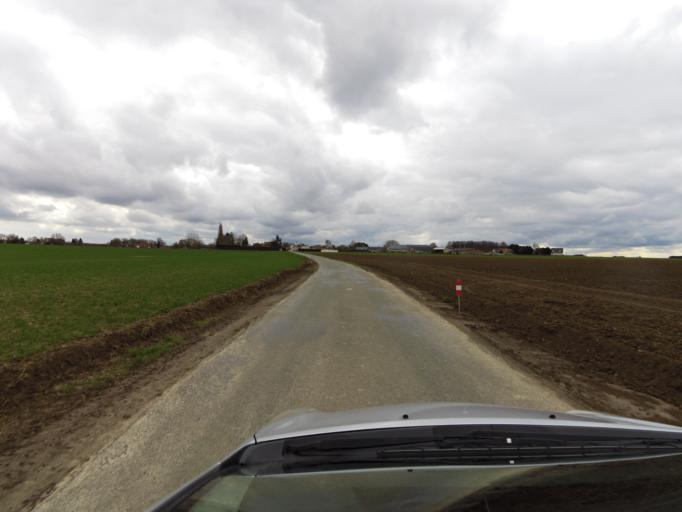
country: FR
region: Picardie
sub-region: Departement de la Somme
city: Bray-sur-Somme
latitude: 49.9146
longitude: 2.8047
